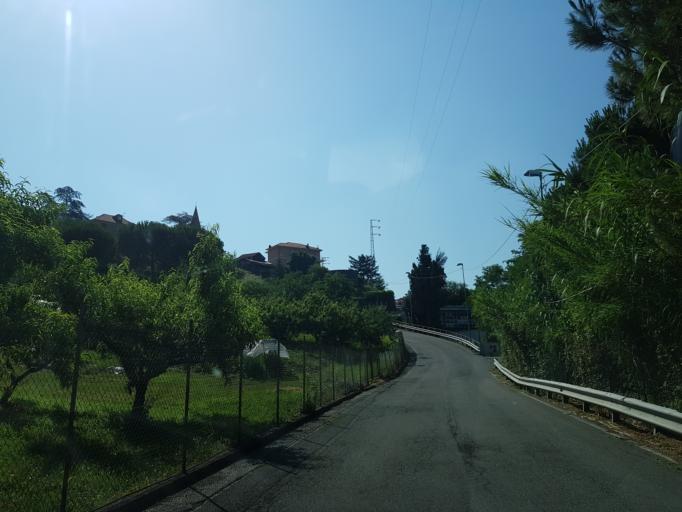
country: IT
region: Liguria
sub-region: Provincia di Genova
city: Pedemonte
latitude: 44.4988
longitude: 8.9103
